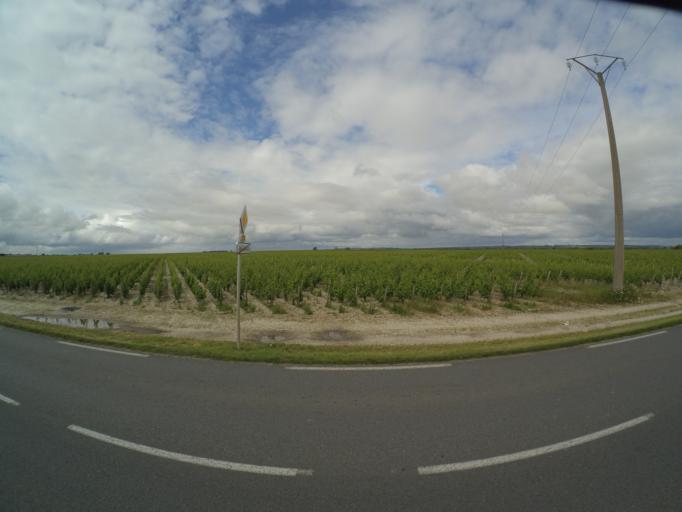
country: FR
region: Aquitaine
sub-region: Departement de la Gironde
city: Margaux
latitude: 45.0450
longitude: -0.6805
